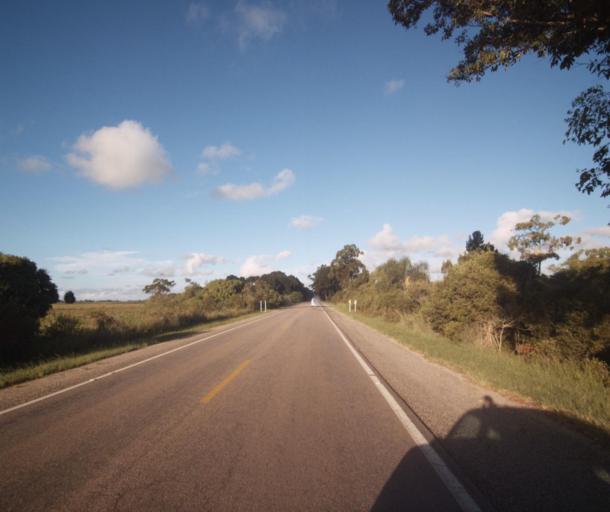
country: BR
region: Rio Grande do Sul
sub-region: Rio Grande
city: Rio Grande
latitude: -32.0957
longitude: -52.3155
